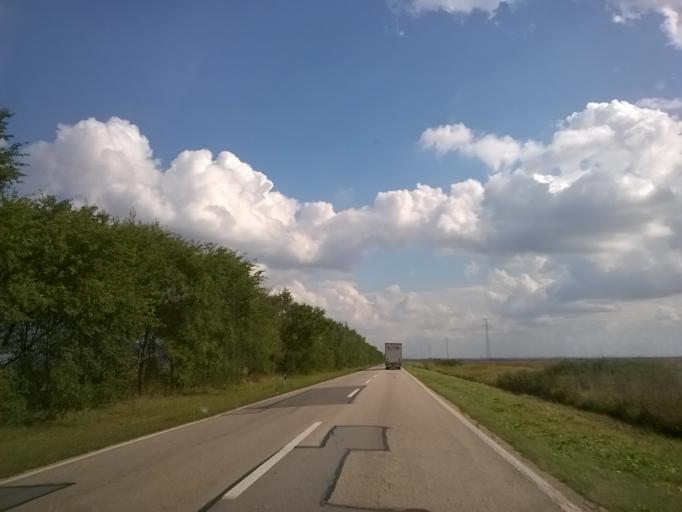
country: RS
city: Margita
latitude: 45.1756
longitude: 21.2178
